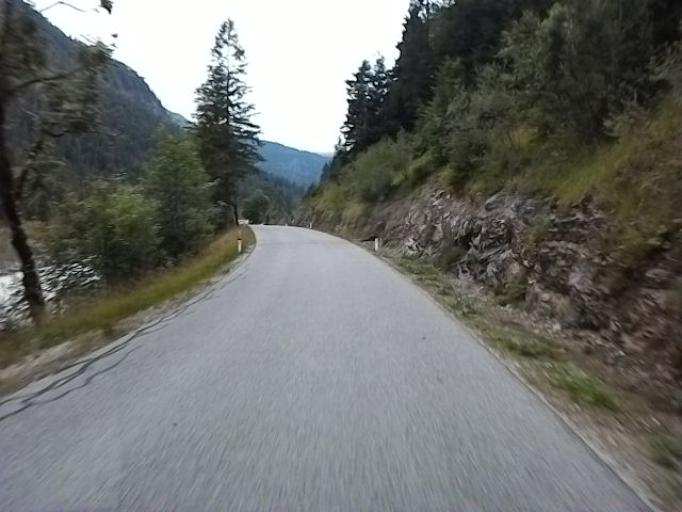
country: DE
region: Bavaria
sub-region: Upper Bavaria
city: Jachenau
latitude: 47.5031
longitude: 11.4553
